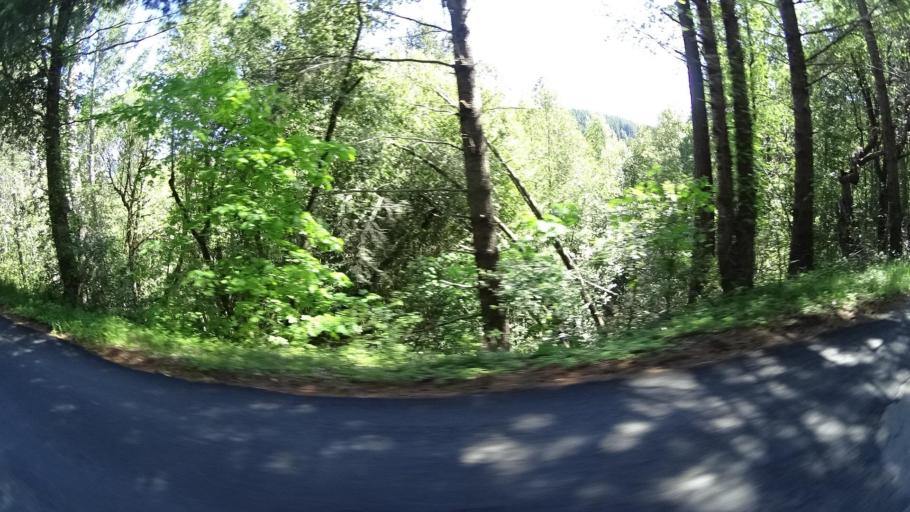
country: US
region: California
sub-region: Humboldt County
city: Rio Dell
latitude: 40.2318
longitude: -124.1536
